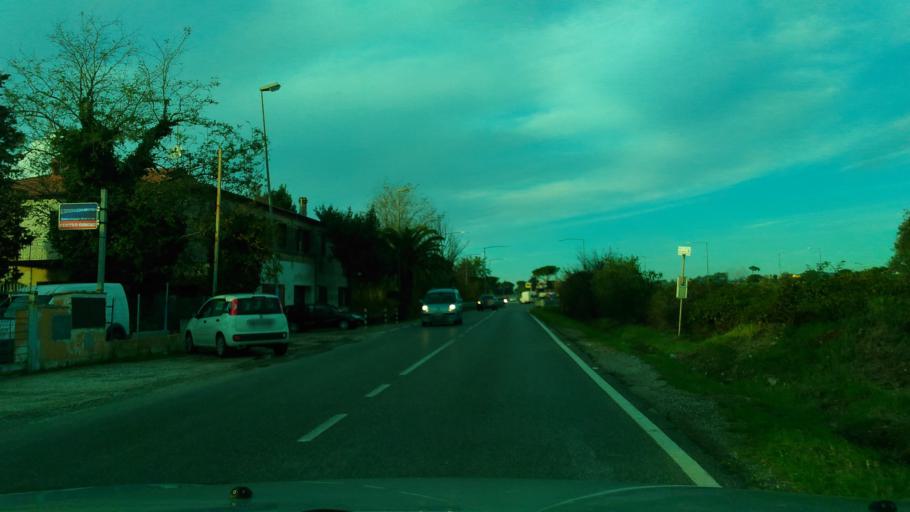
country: IT
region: Tuscany
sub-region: Provincia di Livorno
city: S.P. in Palazzi
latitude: 43.3306
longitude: 10.5066
